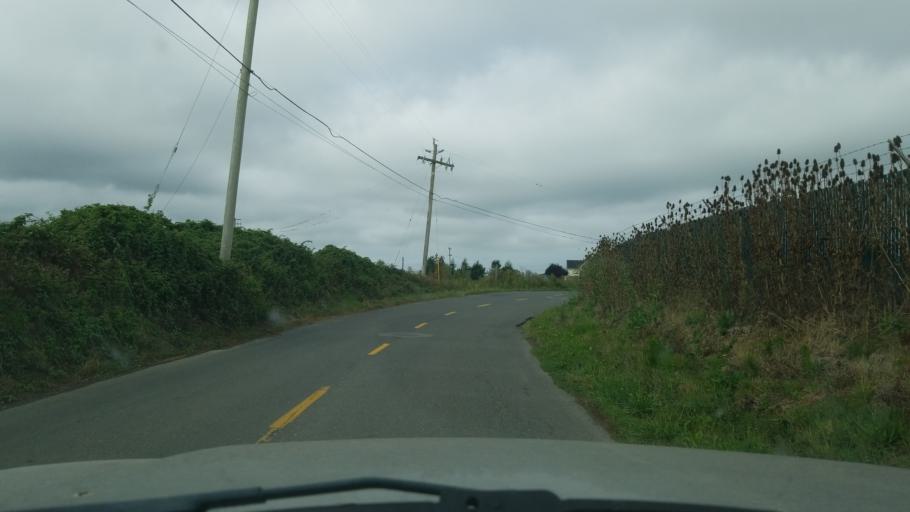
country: US
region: California
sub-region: Humboldt County
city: Ferndale
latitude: 40.5930
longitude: -124.2600
